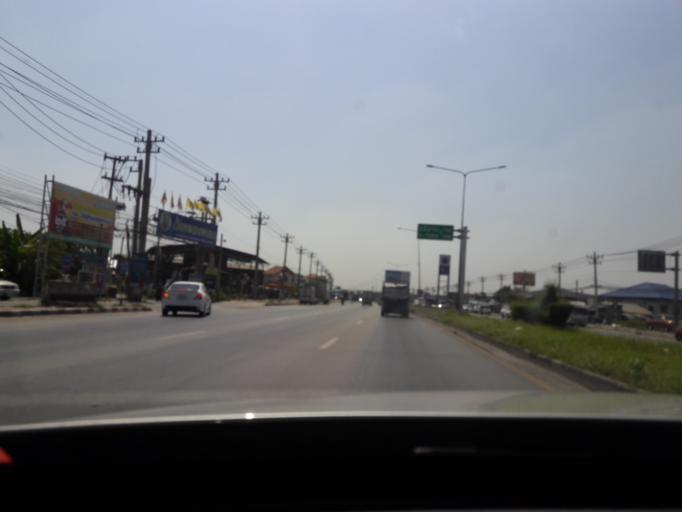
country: TH
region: Bangkok
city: Nong Khaem
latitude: 13.6798
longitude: 100.3207
